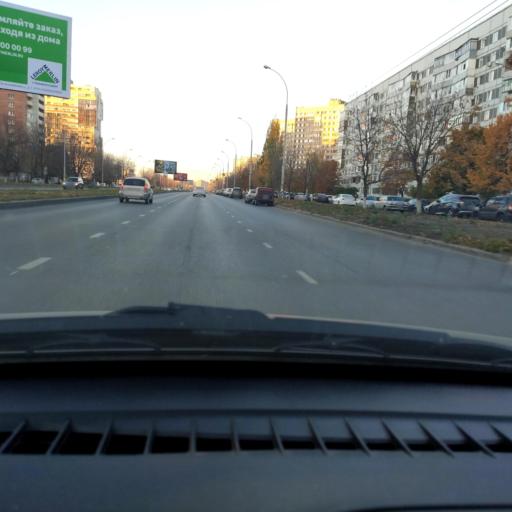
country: RU
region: Samara
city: Tol'yatti
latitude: 53.5298
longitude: 49.3378
